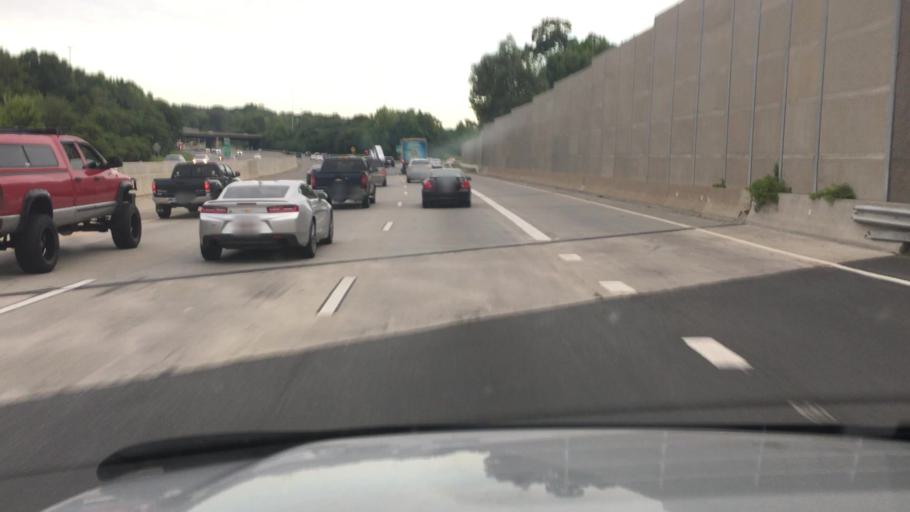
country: US
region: North Carolina
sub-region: Mecklenburg County
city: Pineville
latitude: 35.0983
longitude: -80.8771
